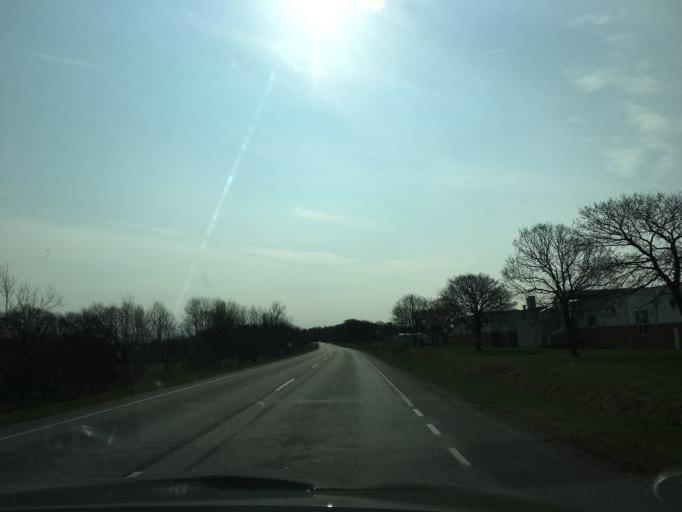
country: DK
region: South Denmark
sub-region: Vejen Kommune
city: Vejen
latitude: 55.4736
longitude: 9.1657
